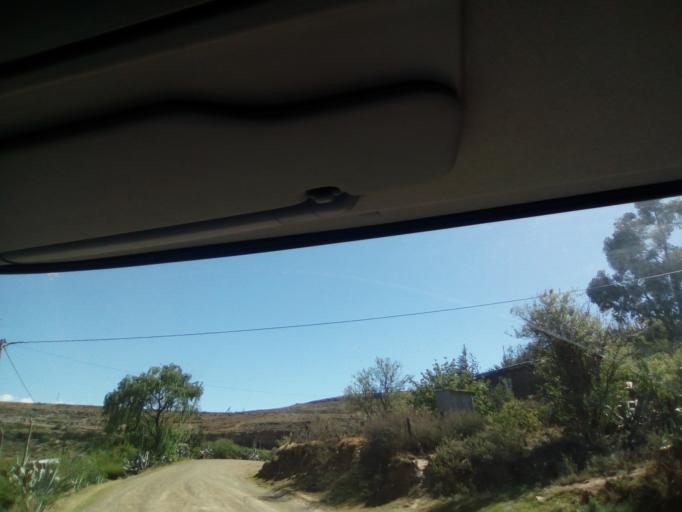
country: LS
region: Qacha's Nek
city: Qacha's Nek
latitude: -30.0437
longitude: 28.6583
